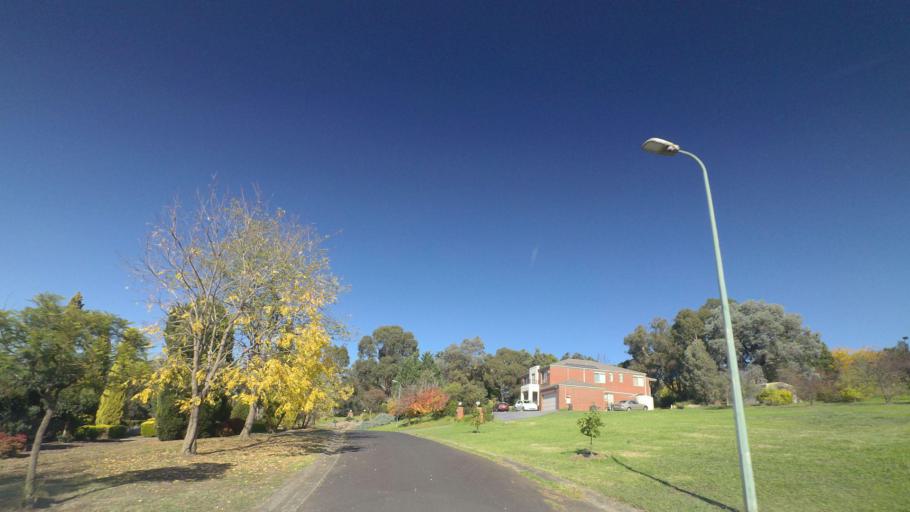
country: AU
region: Victoria
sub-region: Nillumbik
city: Eltham
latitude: -37.7459
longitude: 145.1609
